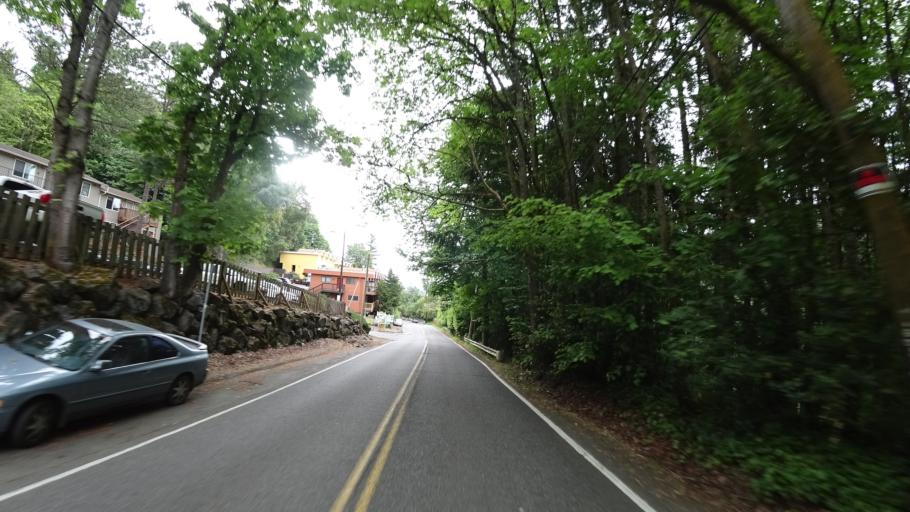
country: US
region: Oregon
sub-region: Multnomah County
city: Portland
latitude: 45.5036
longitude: -122.6894
